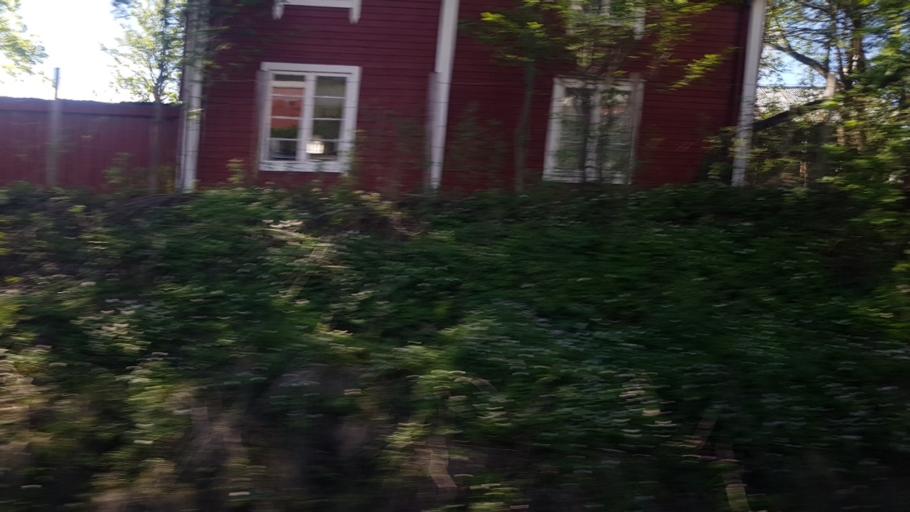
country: NO
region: Sor-Trondelag
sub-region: Midtre Gauldal
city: Storen
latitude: 62.9688
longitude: 10.2036
